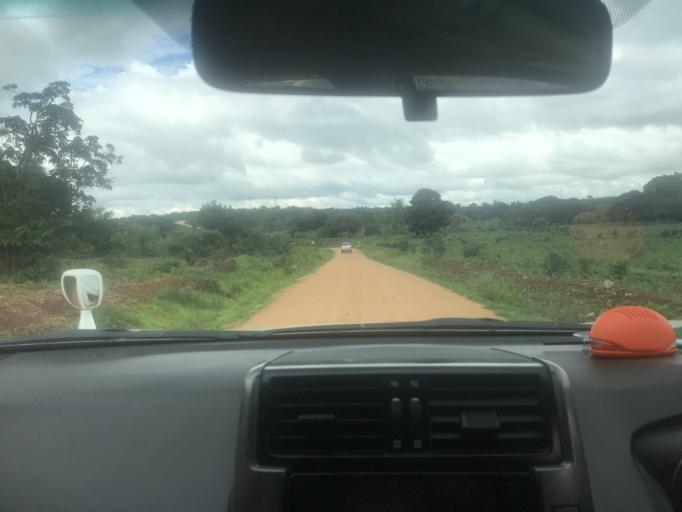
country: TZ
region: Morogoro
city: Kimamba
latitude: -7.0599
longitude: 37.3764
